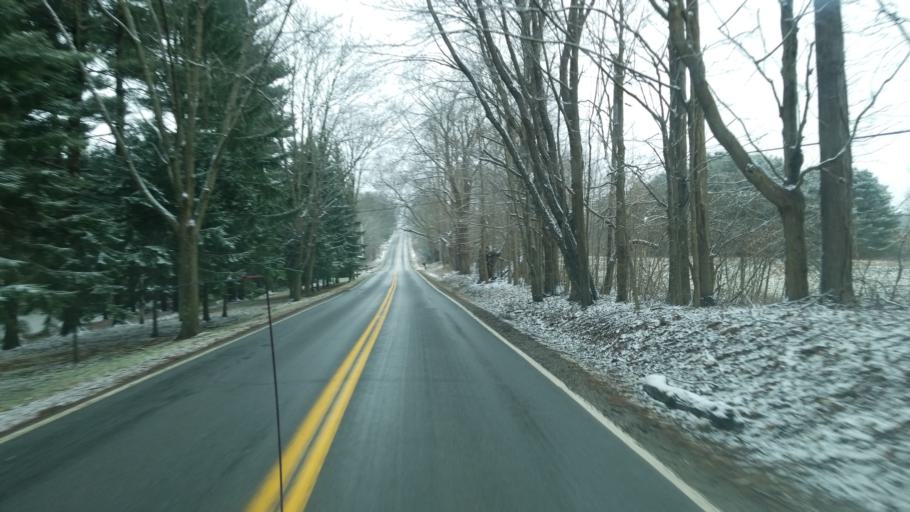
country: US
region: Ohio
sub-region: Portage County
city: Mantua
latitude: 41.2841
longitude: -81.2518
